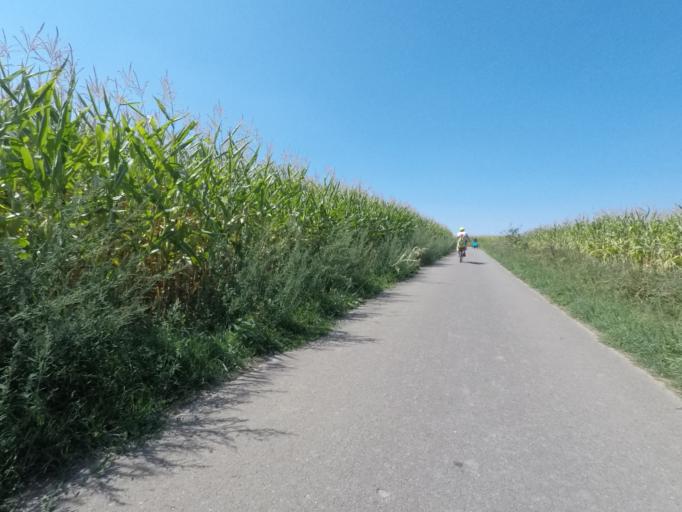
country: LU
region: Luxembourg
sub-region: Canton de Capellen
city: Steinfort
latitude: 49.6339
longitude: 5.9288
